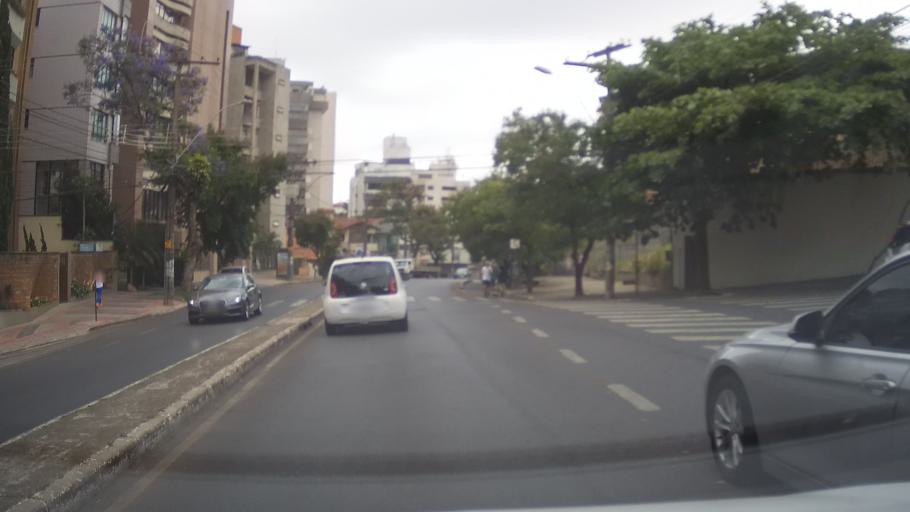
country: BR
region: Minas Gerais
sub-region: Belo Horizonte
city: Belo Horizonte
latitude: -19.9530
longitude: -43.9245
